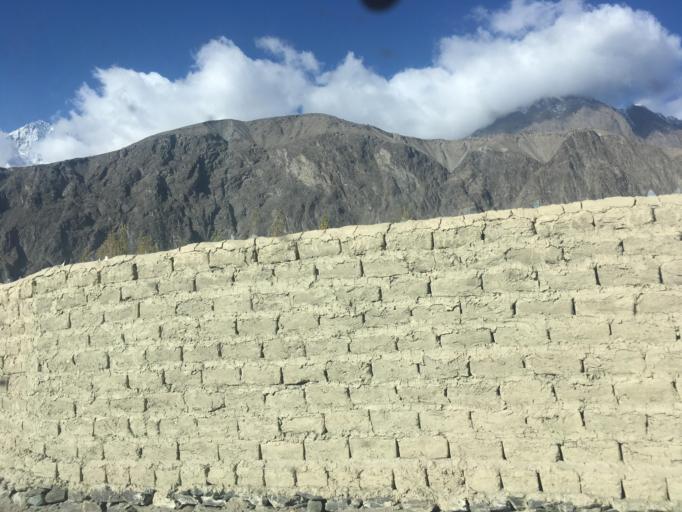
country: PK
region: Gilgit-Baltistan
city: Skardu
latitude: 35.3500
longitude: 75.5242
